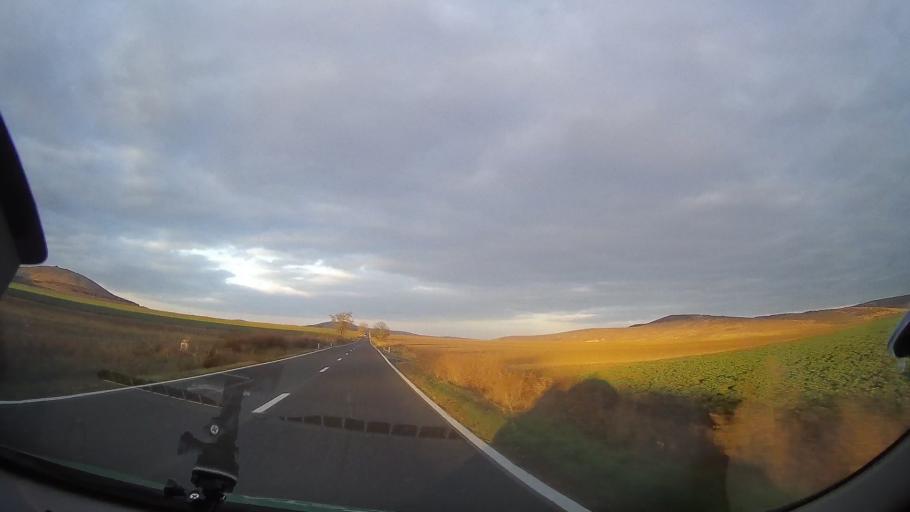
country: RO
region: Tulcea
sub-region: Comuna Nalbant
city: Nicolae Balcescu
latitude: 44.9724
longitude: 28.5410
